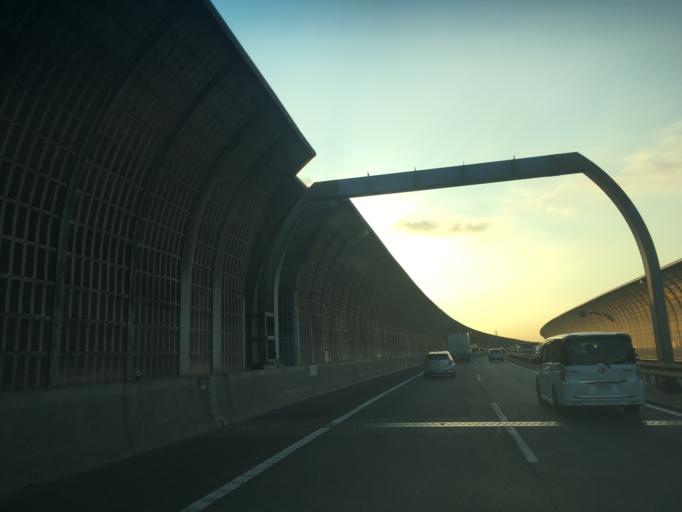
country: JP
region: Saitama
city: Soka
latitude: 35.8515
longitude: 139.8068
